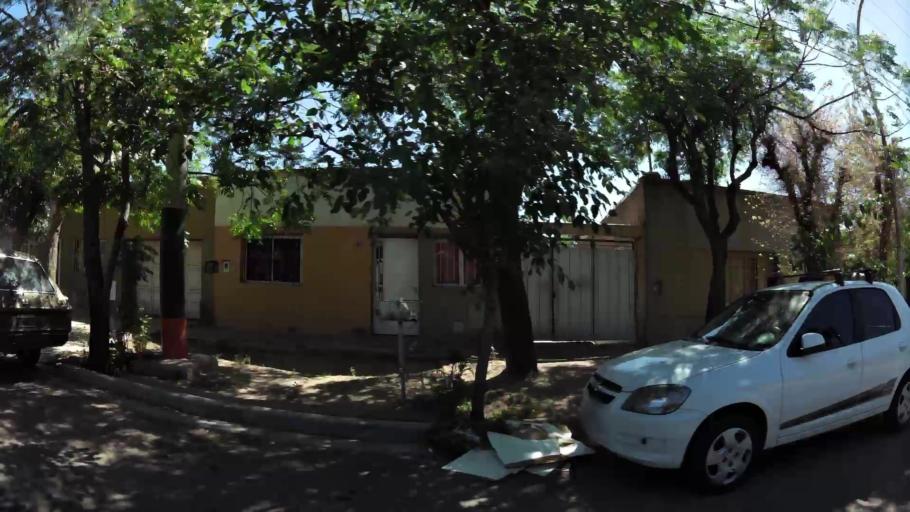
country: AR
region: Mendoza
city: Villa Nueva
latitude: -32.8986
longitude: -68.7787
